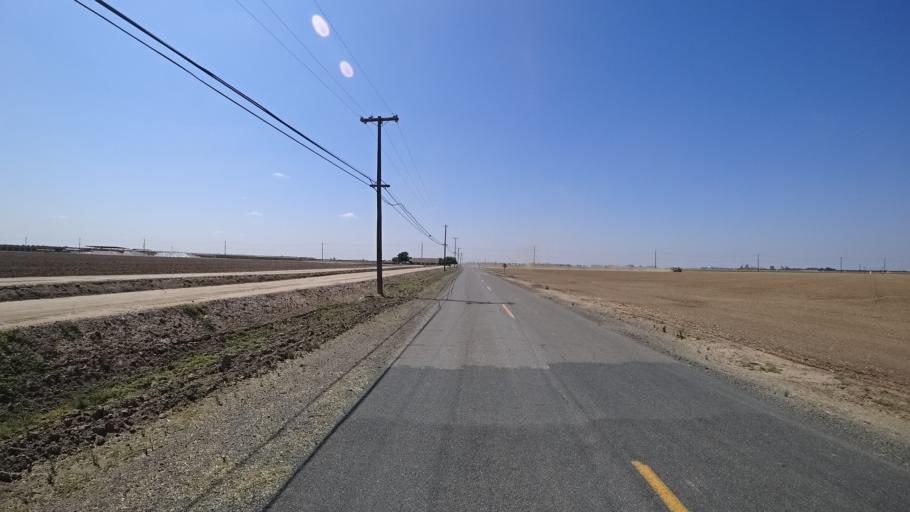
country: US
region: California
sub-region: Kings County
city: Home Garden
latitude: 36.2574
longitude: -119.6189
